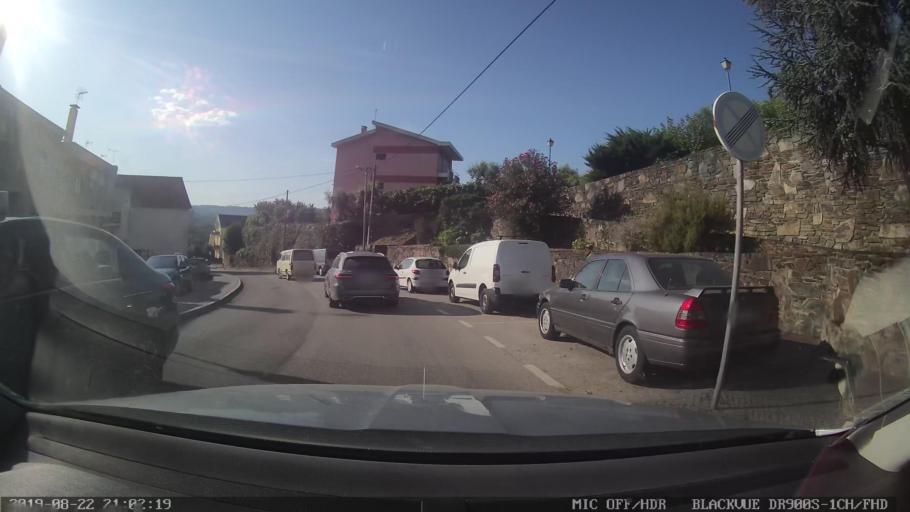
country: PT
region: Castelo Branco
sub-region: Serta
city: Serta
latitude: 39.8092
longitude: -8.0978
